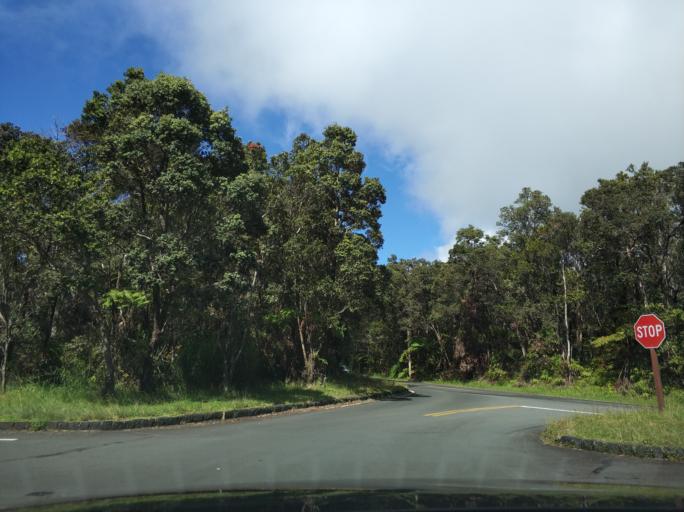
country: US
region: Hawaii
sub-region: Hawaii County
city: Volcano
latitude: 19.4168
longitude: -155.2429
